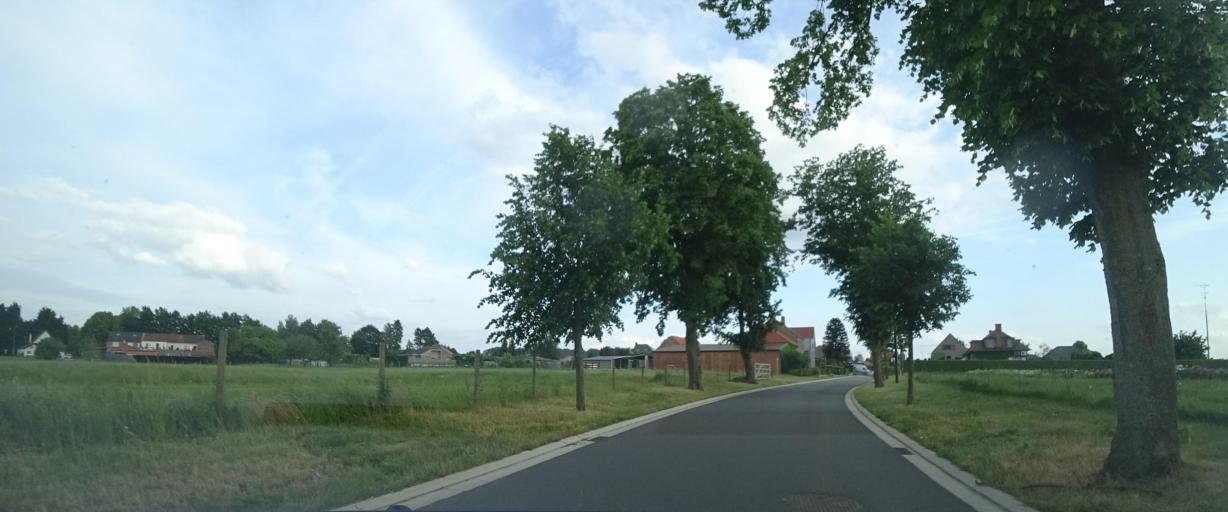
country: BE
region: Flanders
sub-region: Provincie Limburg
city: Nieuwerkerken
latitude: 50.8705
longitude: 5.1949
